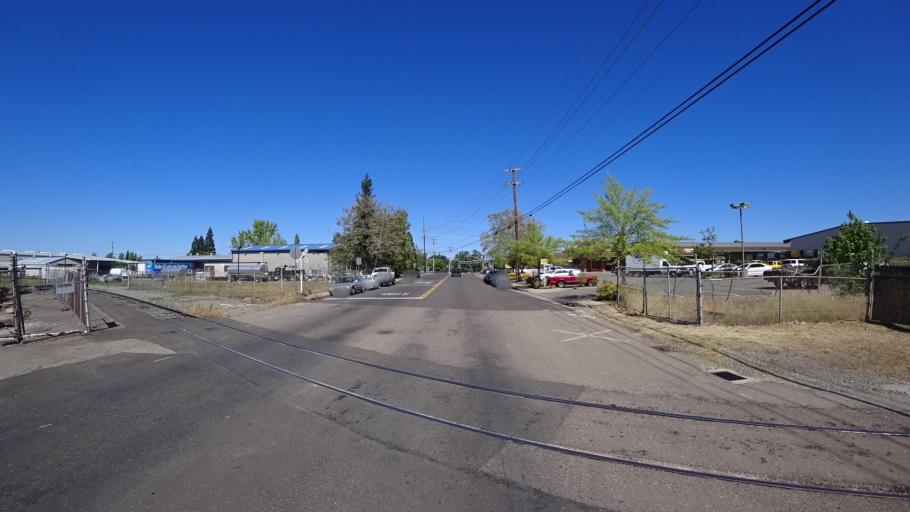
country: US
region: California
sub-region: Placer County
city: Rocklin
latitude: 38.8033
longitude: -121.2179
